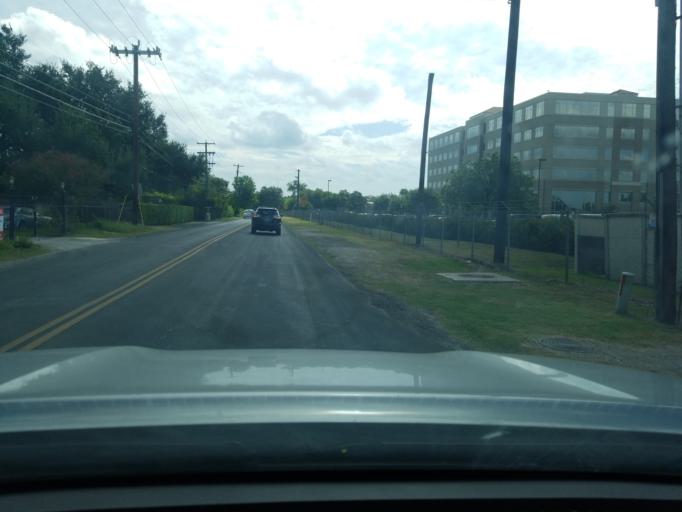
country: US
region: Texas
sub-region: Bexar County
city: Terrell Hills
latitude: 29.4683
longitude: -98.4516
